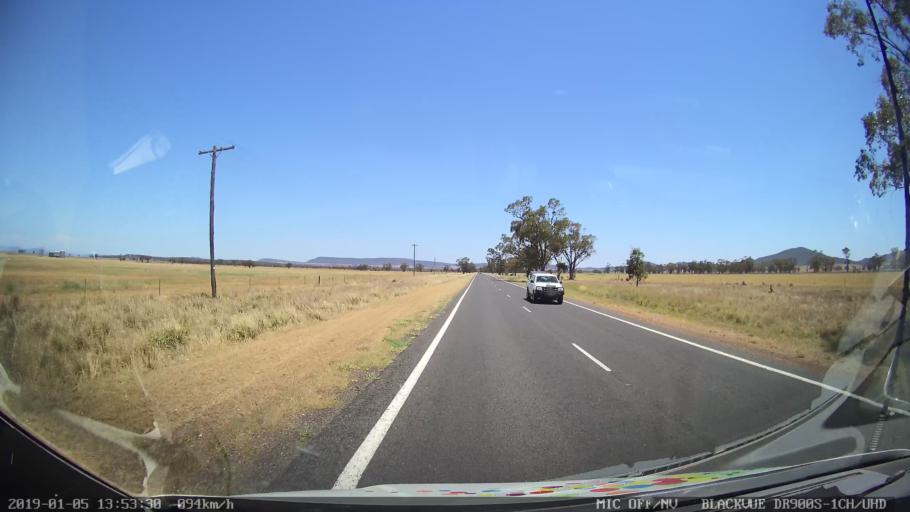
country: AU
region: New South Wales
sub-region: Gunnedah
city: Gunnedah
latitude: -31.0757
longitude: 150.2772
